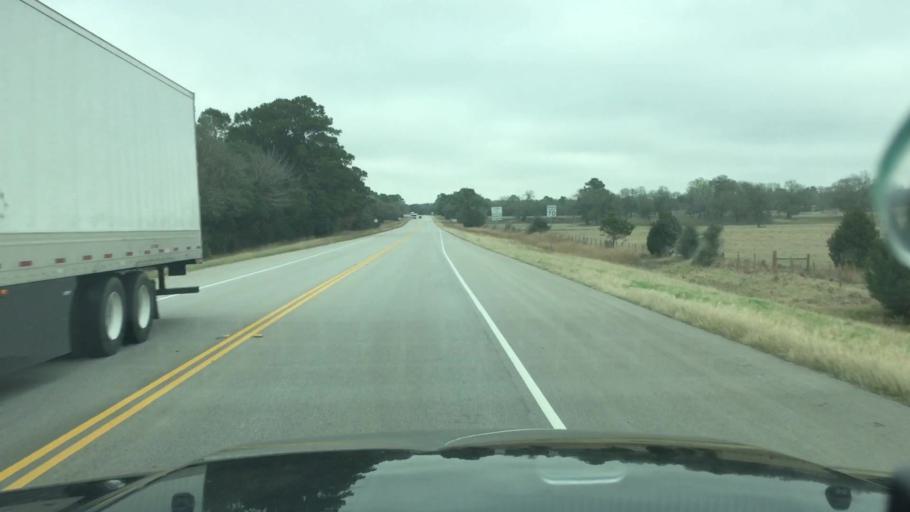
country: US
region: Texas
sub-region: Lee County
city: Giddings
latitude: 30.0853
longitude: -96.9160
